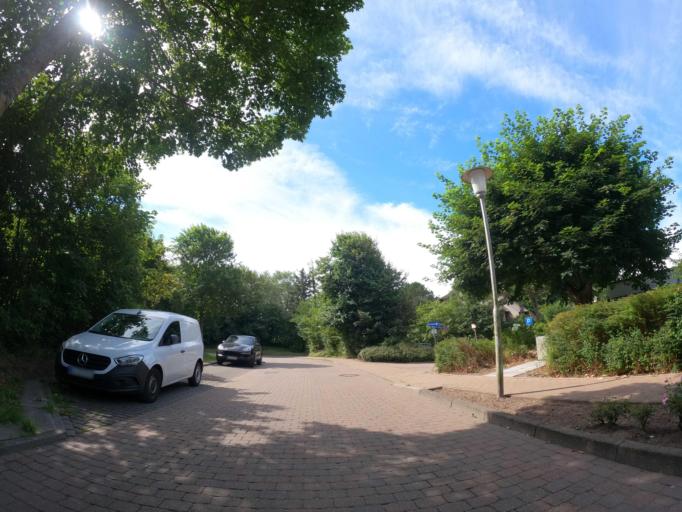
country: DE
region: Schleswig-Holstein
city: Tinnum
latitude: 54.9101
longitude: 8.3212
